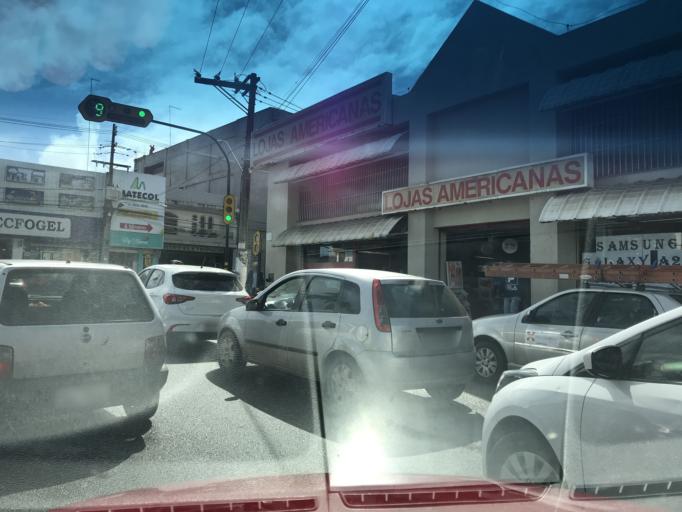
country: BR
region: Bahia
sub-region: Santo Antonio De Jesus
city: Santo Antonio de Jesus
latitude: -12.9663
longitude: -39.2632
